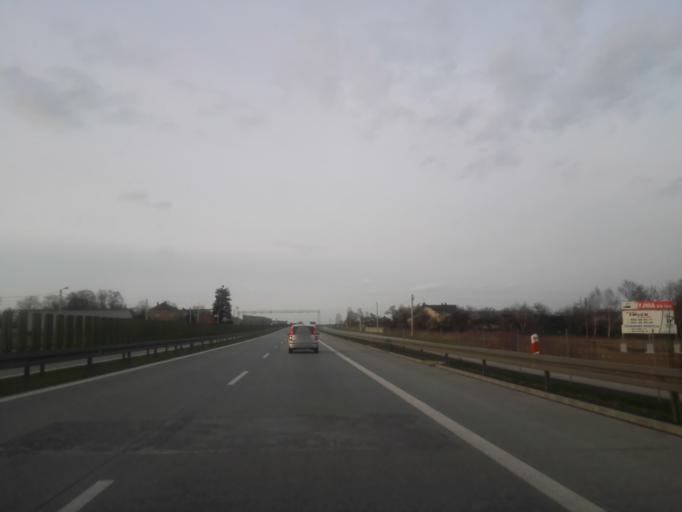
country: PL
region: Lodz Voivodeship
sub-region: Powiat rawski
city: Rawa Mazowiecka
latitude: 51.7396
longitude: 20.2341
